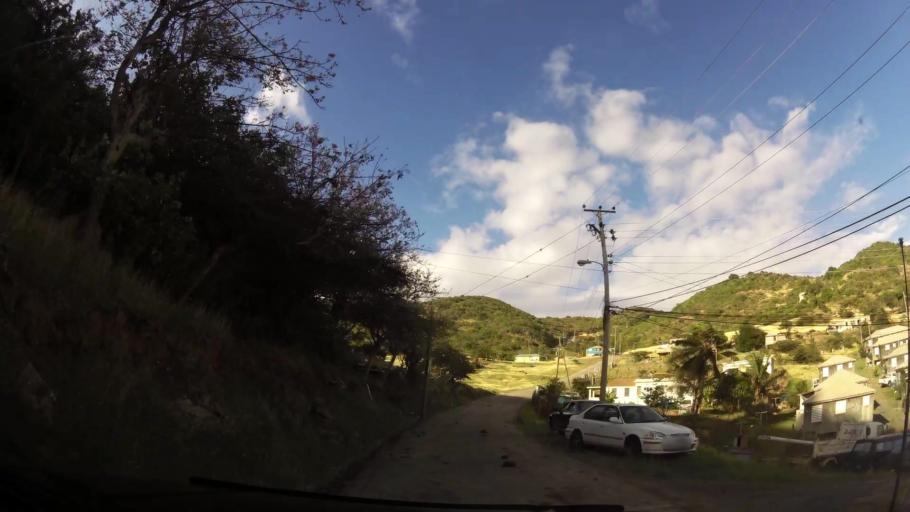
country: MS
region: Saint Peter
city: Brades
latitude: 16.7987
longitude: -62.1947
